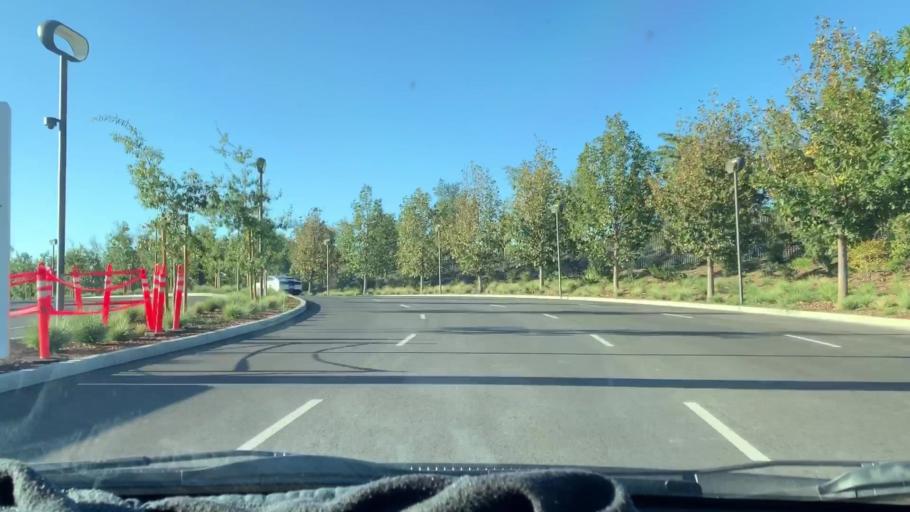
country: US
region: California
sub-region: Santa Clara County
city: Cupertino
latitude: 37.3347
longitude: -122.0125
